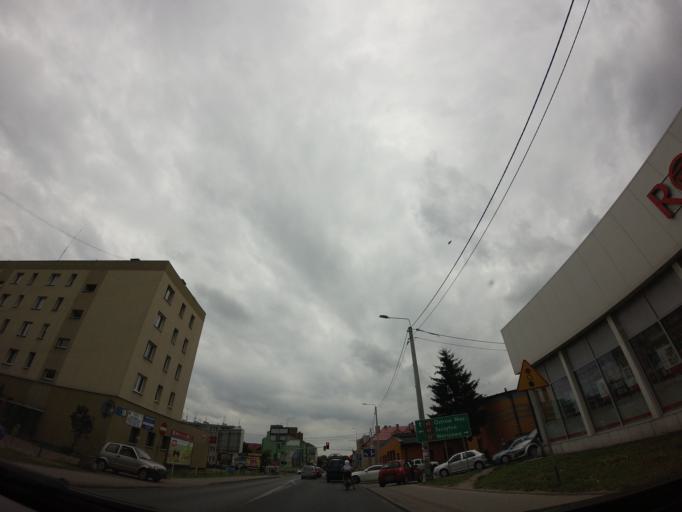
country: PL
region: Masovian Voivodeship
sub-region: Powiat makowski
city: Makow Mazowiecki
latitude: 52.8650
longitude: 21.0996
